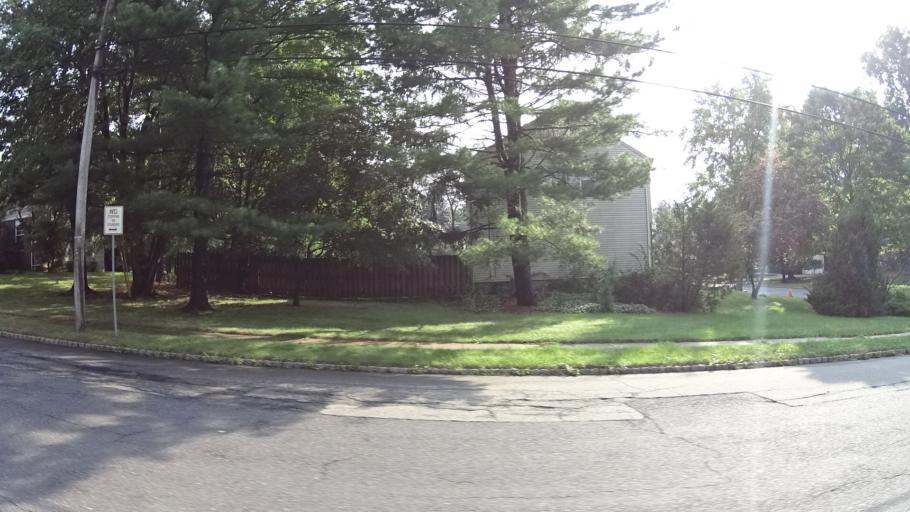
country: US
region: New Jersey
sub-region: Union County
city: New Providence
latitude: 40.6987
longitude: -74.4217
